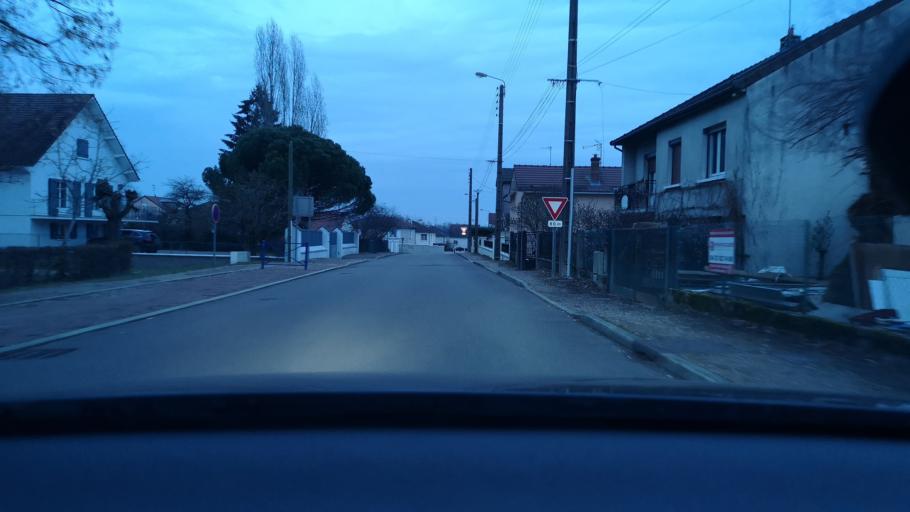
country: FR
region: Bourgogne
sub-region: Departement de Saone-et-Loire
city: Saint-Remy
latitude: 46.7704
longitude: 4.8270
